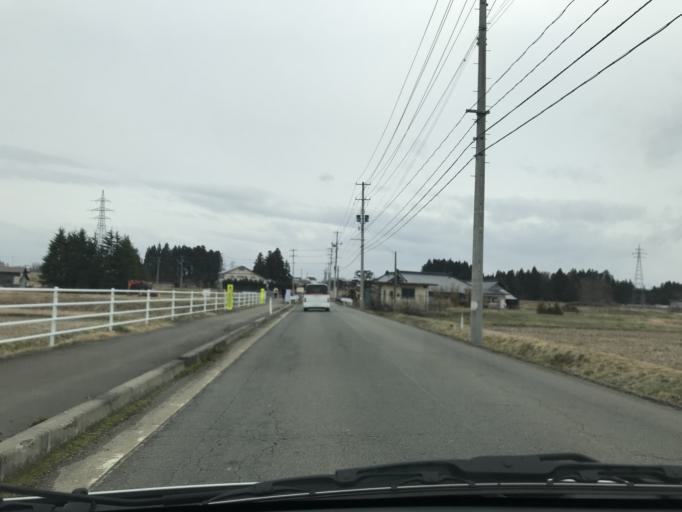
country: JP
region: Iwate
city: Hanamaki
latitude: 39.3471
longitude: 141.0997
